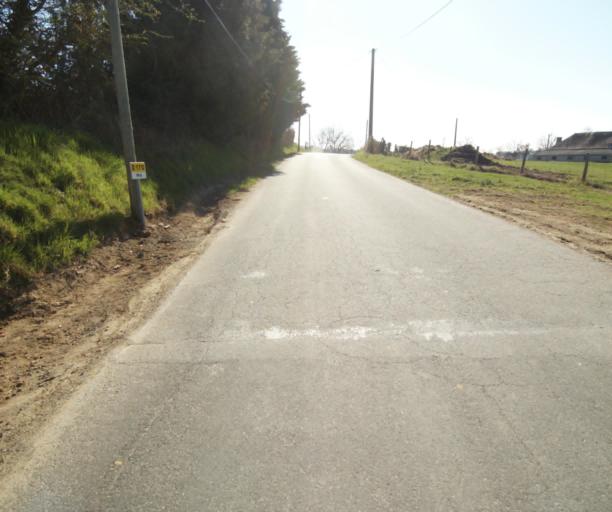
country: FR
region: Limousin
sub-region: Departement de la Correze
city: Saint-Mexant
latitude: 45.2821
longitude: 1.6206
